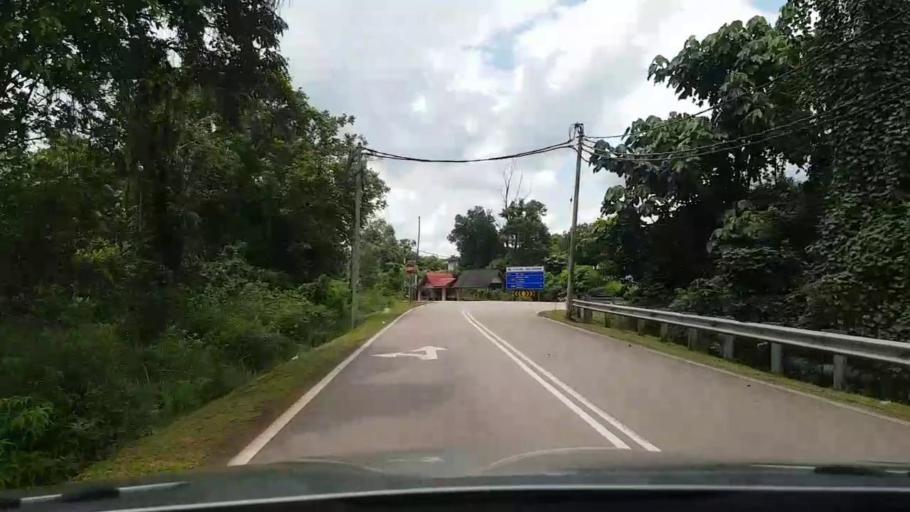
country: MY
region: Pahang
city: Pekan
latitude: 3.1584
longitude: 102.9724
